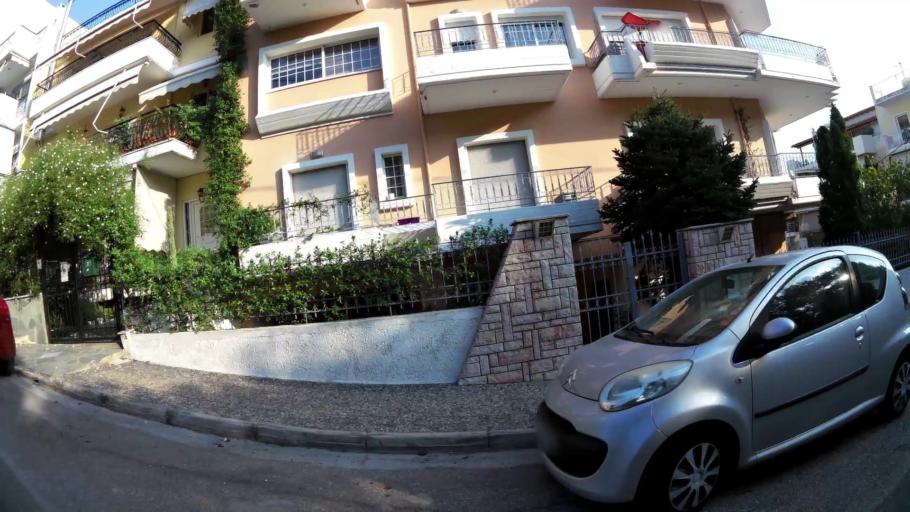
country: GR
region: Attica
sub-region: Nomarchia Athinas
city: Petroupolis
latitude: 38.0472
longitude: 23.6767
